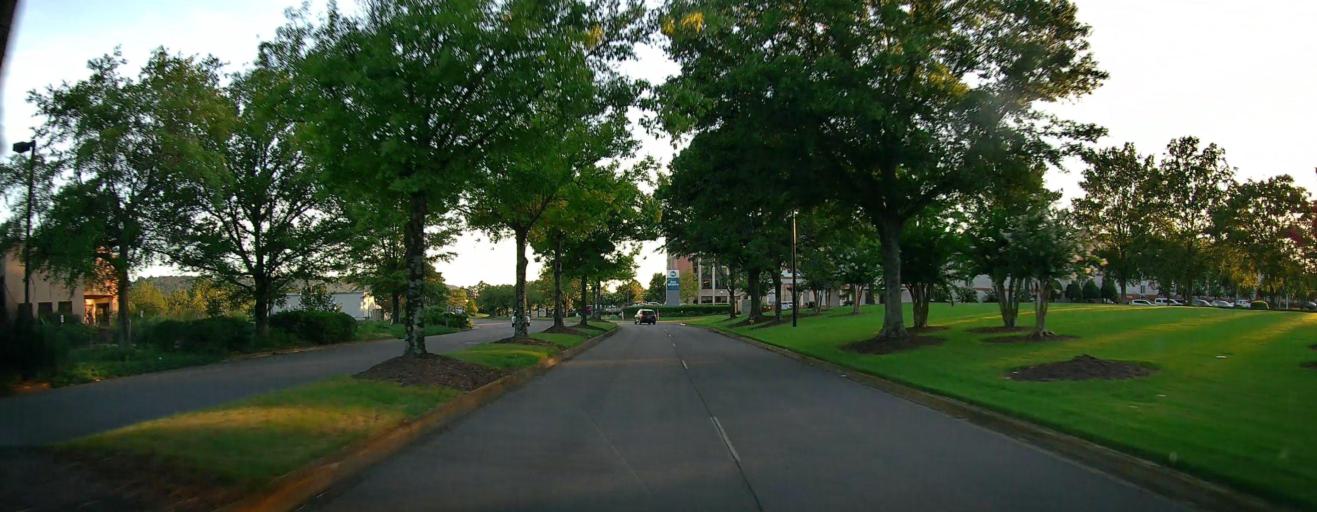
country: US
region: Alabama
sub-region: Jefferson County
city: Homewood
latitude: 33.4511
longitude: -86.8215
